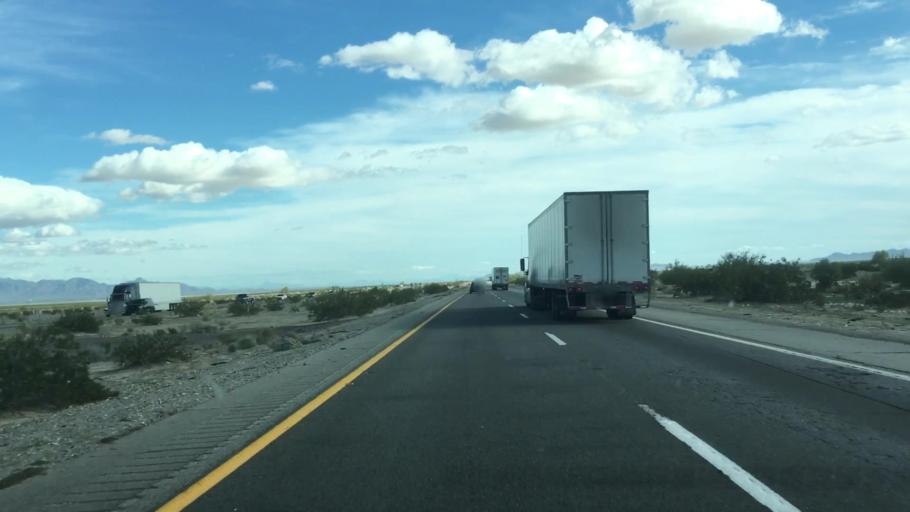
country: US
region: California
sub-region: Riverside County
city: Mesa Verde
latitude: 33.6470
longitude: -115.1240
